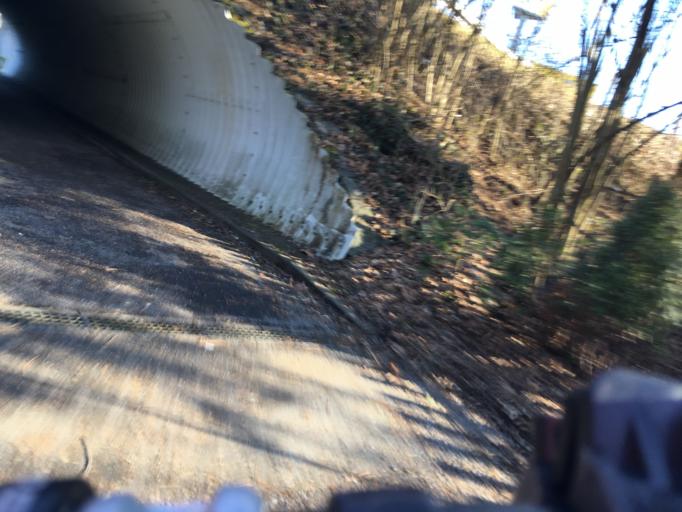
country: DE
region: Baden-Wuerttemberg
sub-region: Freiburg Region
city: Hilzingen
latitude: 47.7616
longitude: 8.7920
